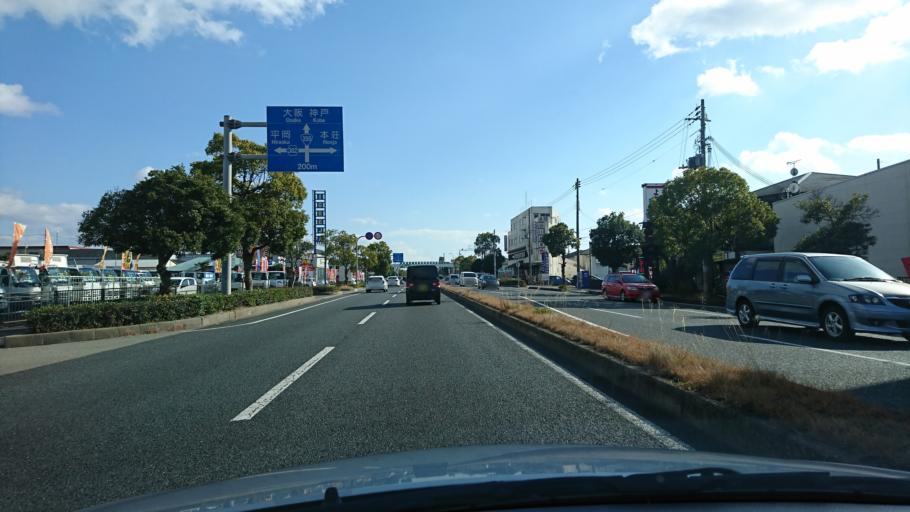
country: JP
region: Hyogo
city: Kakogawacho-honmachi
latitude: 34.7268
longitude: 134.8644
